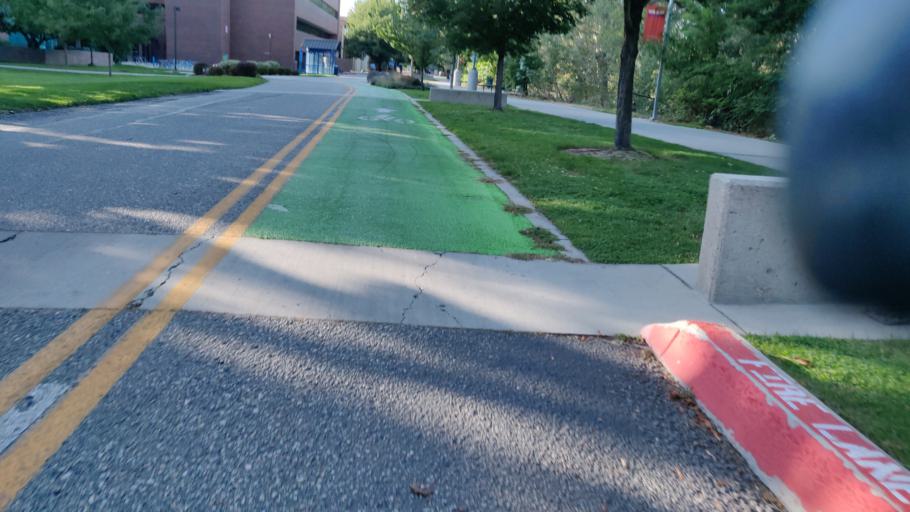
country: US
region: Idaho
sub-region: Ada County
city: Boise
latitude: 43.6056
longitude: -116.2047
